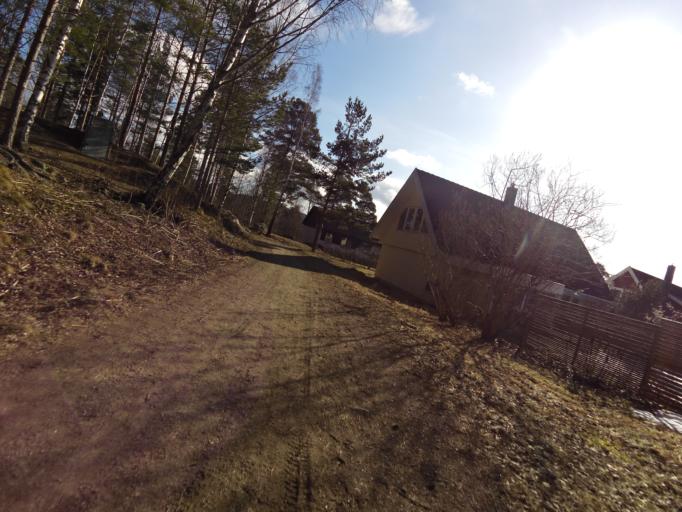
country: SE
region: Gaevleborg
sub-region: Hofors Kommun
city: Hofors
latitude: 60.5524
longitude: 16.2842
